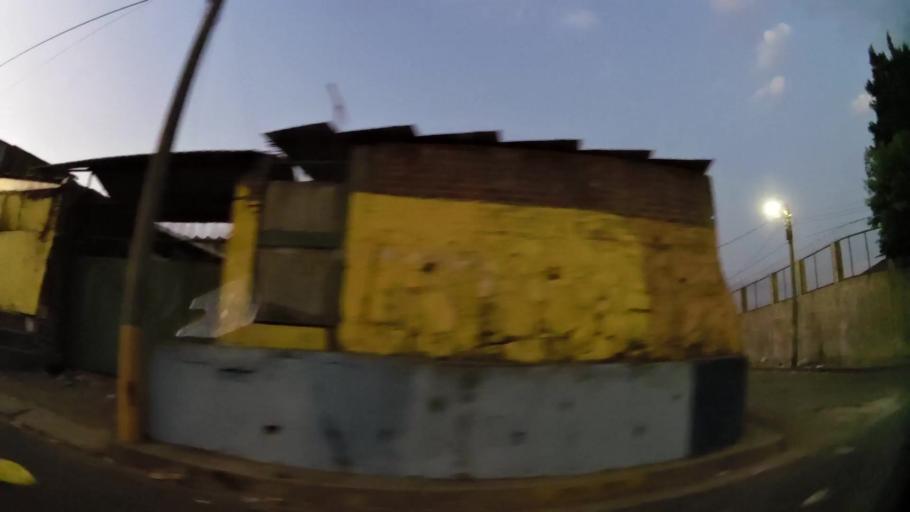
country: SV
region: San Salvador
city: San Salvador
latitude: 13.7084
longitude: -89.1885
